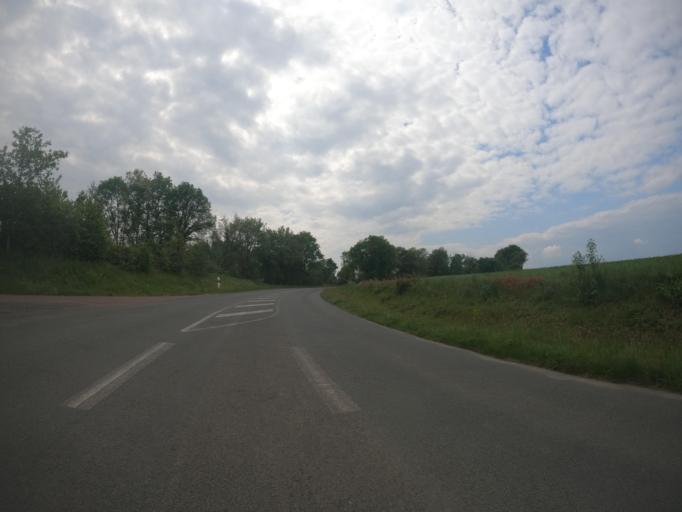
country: FR
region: Poitou-Charentes
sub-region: Departement des Deux-Sevres
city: Saint-Varent
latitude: 46.8803
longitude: -0.2635
